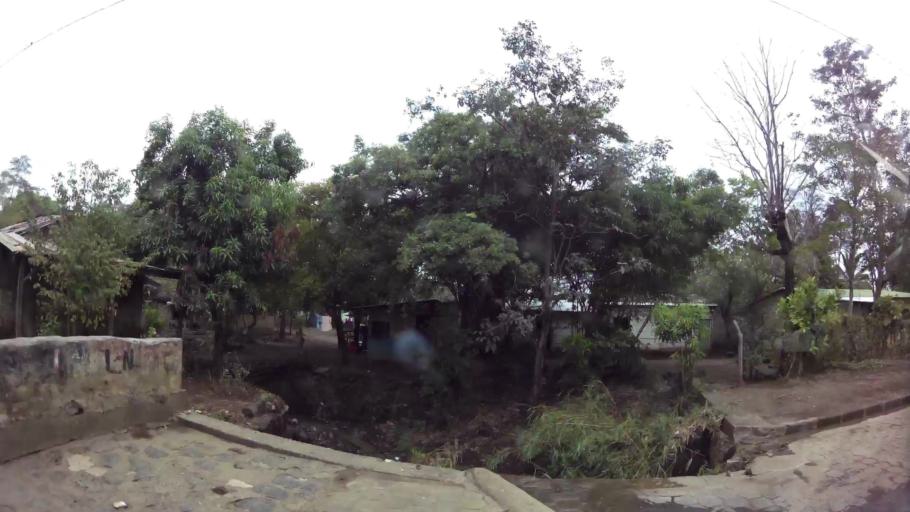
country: NI
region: Granada
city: Nandaime
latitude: 11.7545
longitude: -86.0481
